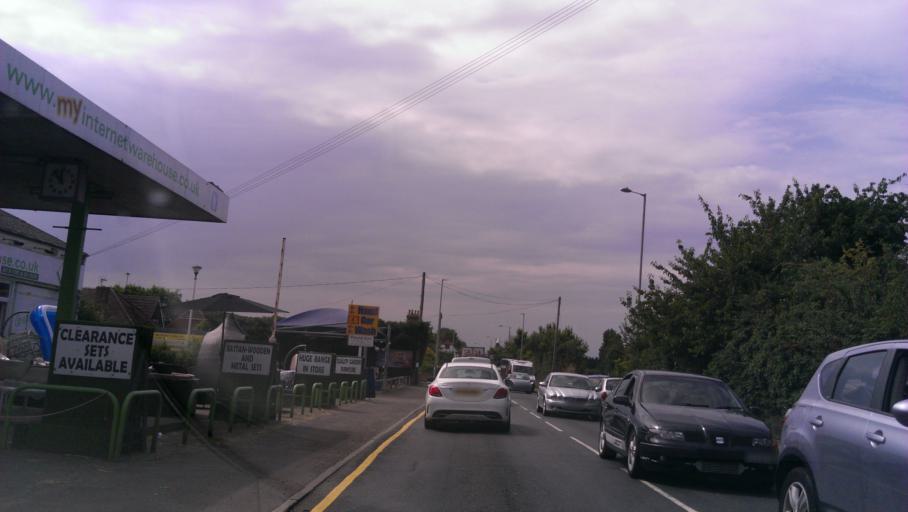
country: GB
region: England
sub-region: Kent
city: Teynham
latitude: 51.3294
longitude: 0.7930
